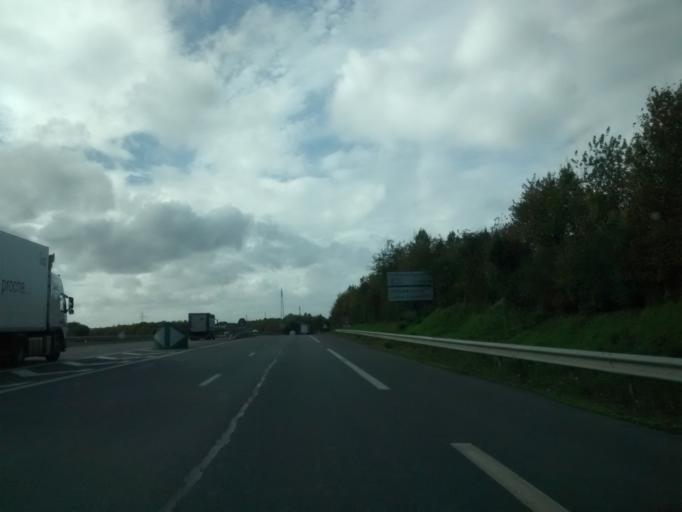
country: FR
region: Brittany
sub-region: Departement d'Ille-et-Vilaine
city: Acigne
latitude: 48.1149
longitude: -1.5616
